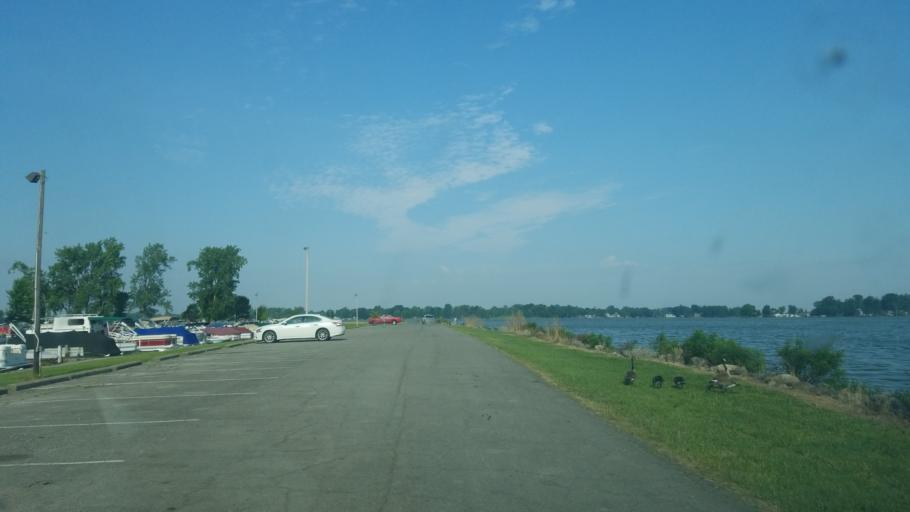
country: US
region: Ohio
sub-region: Logan County
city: Russells Point
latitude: 40.4800
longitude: -83.8651
